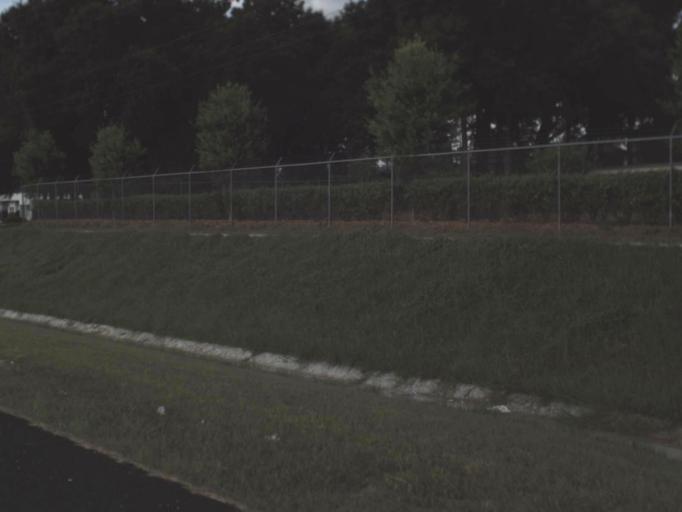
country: US
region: Florida
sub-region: Pasco County
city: Dade City North
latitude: 28.3907
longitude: -82.1947
